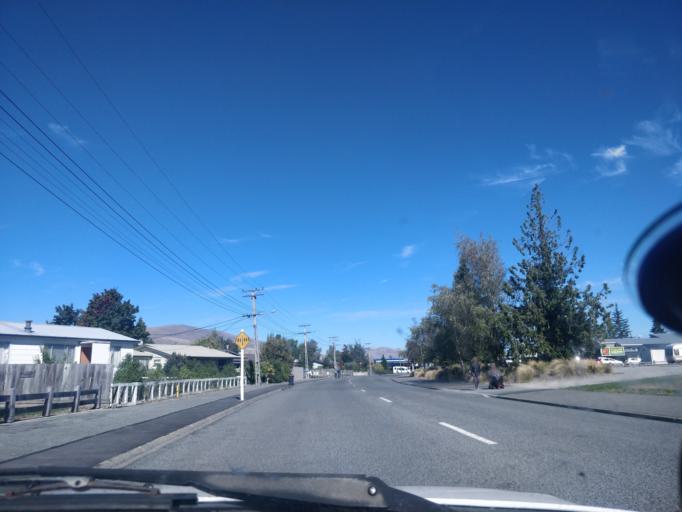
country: NZ
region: Canterbury
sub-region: Timaru District
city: Pleasant Point
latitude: -44.2558
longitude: 170.1012
